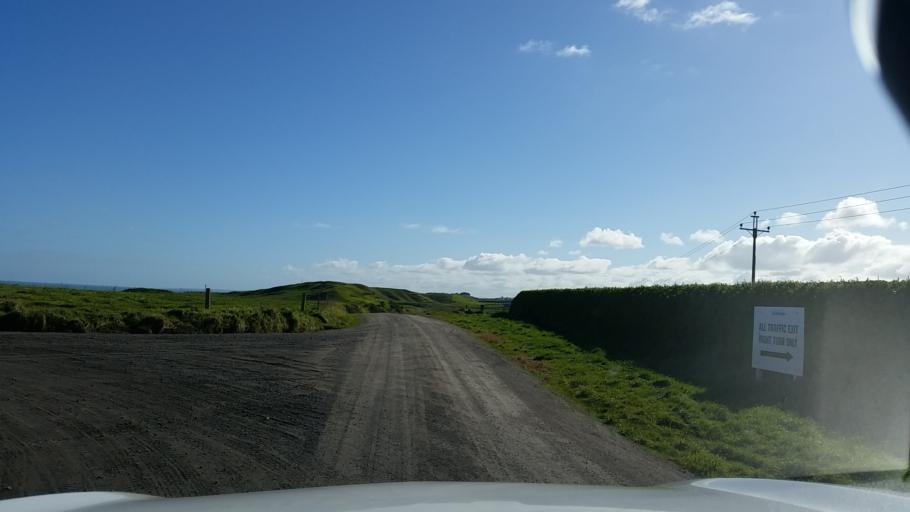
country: NZ
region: Taranaki
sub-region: South Taranaki District
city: Patea
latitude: -39.6862
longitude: 174.3953
